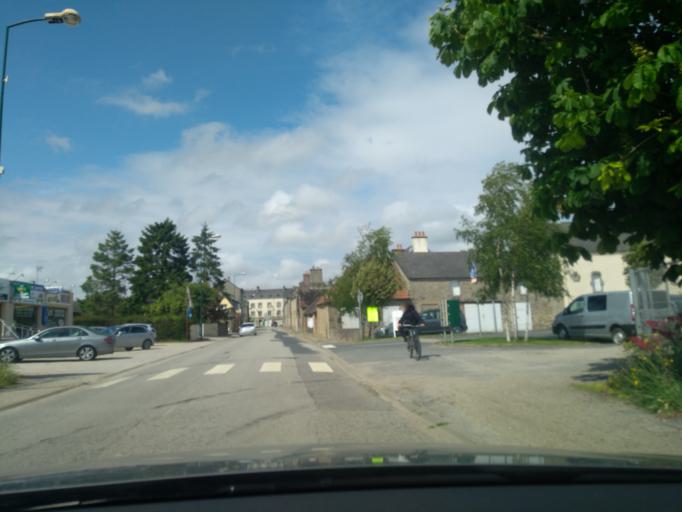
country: FR
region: Lower Normandy
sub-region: Departement de la Manche
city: Quettehou
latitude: 49.5908
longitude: -1.3021
